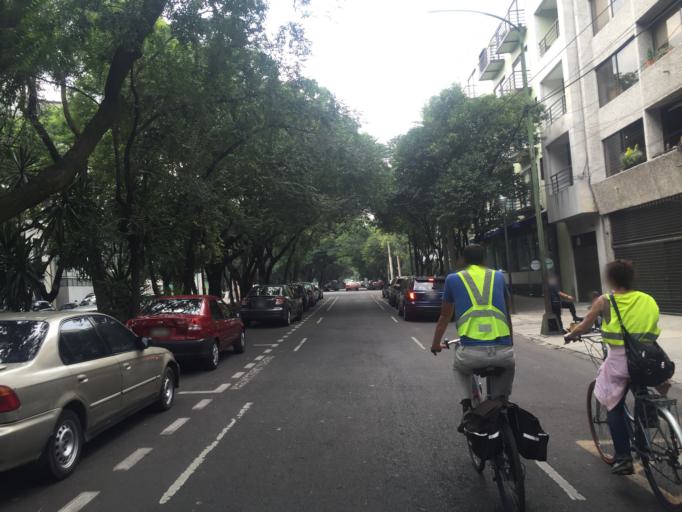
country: MX
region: Mexico City
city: Benito Juarez
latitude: 19.4166
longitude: -99.1727
